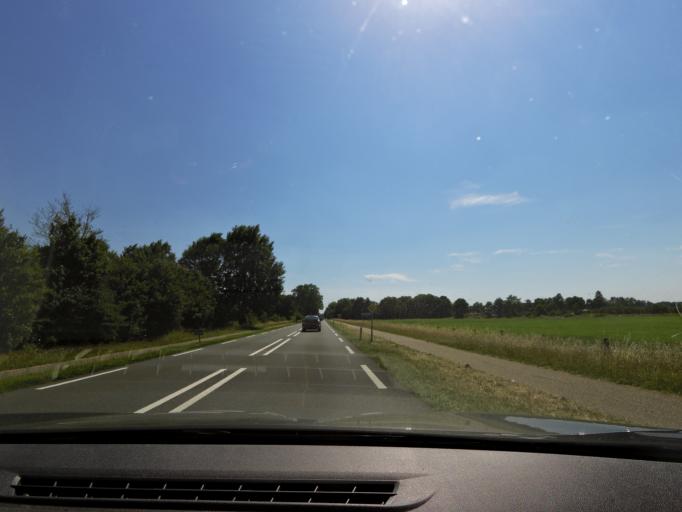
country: NL
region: Gelderland
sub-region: Berkelland
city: Eibergen
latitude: 52.0767
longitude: 6.6361
